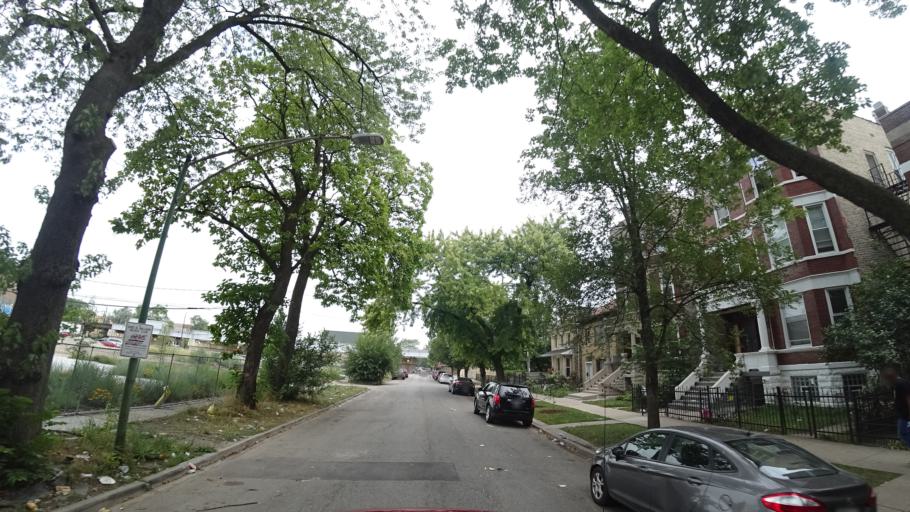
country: US
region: Illinois
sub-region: Cook County
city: Cicero
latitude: 41.8529
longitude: -87.7163
